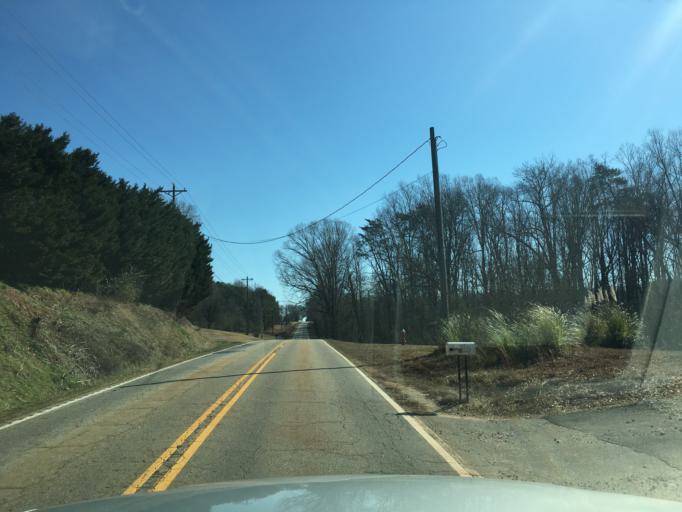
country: US
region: South Carolina
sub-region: Pickens County
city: Liberty
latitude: 34.8007
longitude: -82.7440
